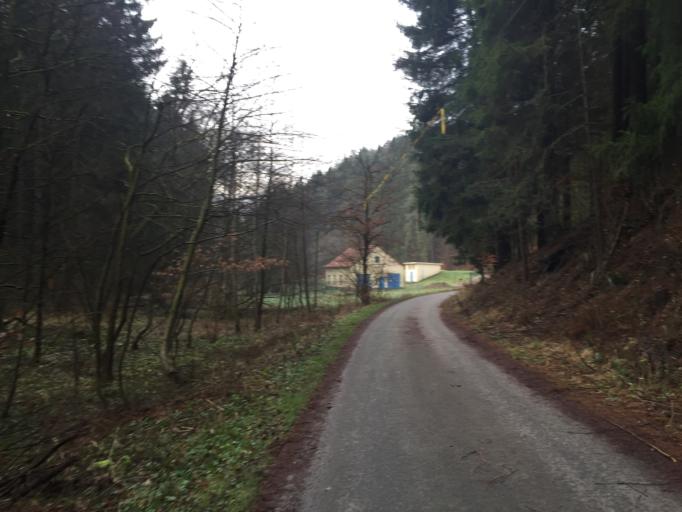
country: DE
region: Thuringia
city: Schleifreisen
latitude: 50.8906
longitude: 11.8160
